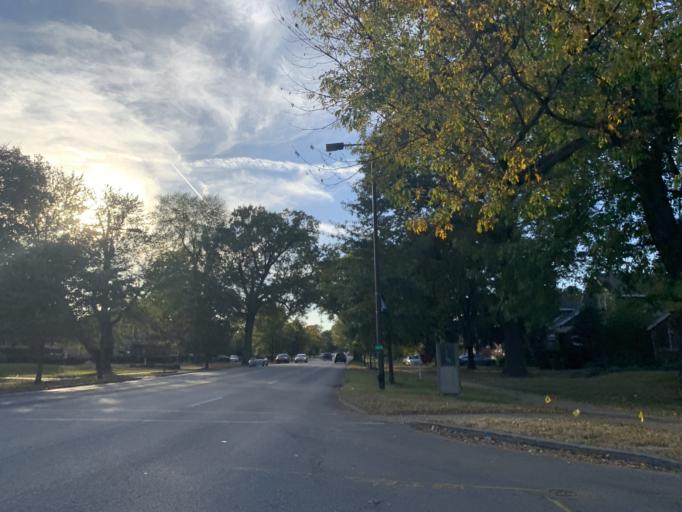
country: US
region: Kentucky
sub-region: Jefferson County
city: Shively
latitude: 38.2233
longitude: -85.7925
